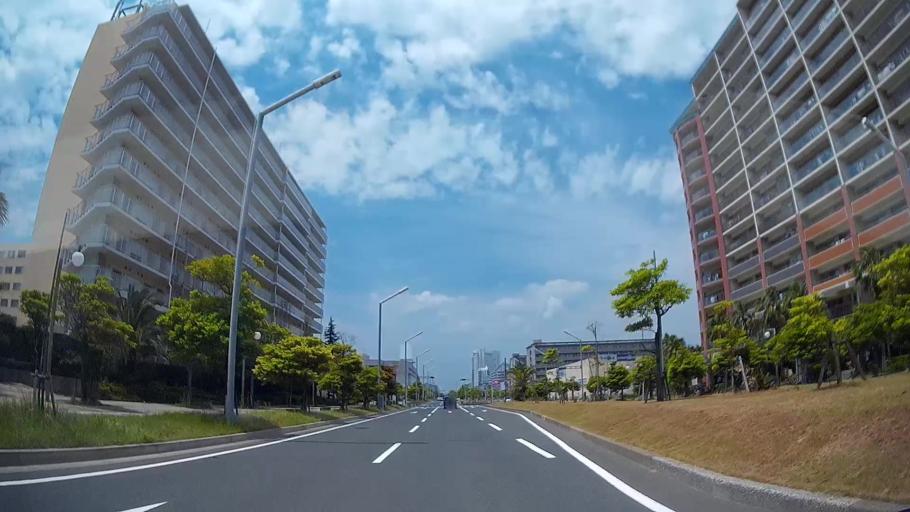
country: JP
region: Tokyo
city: Urayasu
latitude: 35.6409
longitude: 139.9266
